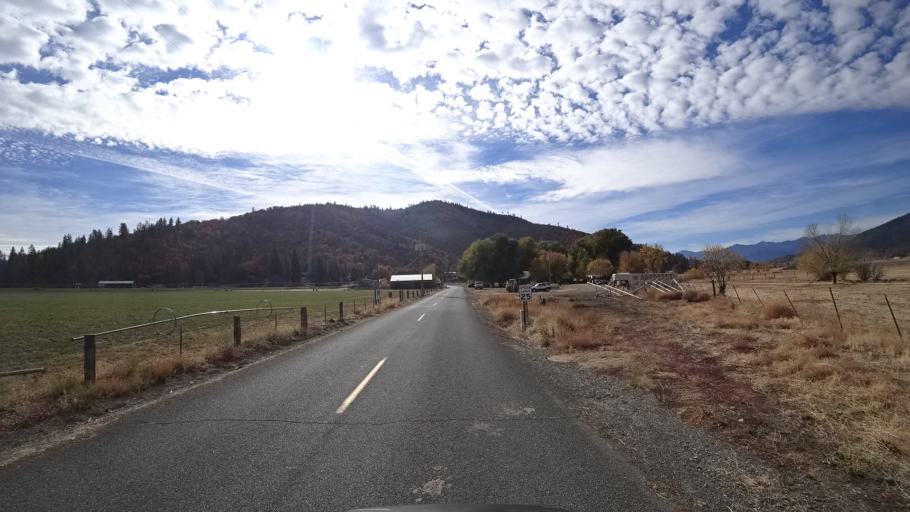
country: US
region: California
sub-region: Siskiyou County
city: Yreka
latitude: 41.6271
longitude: -122.8283
